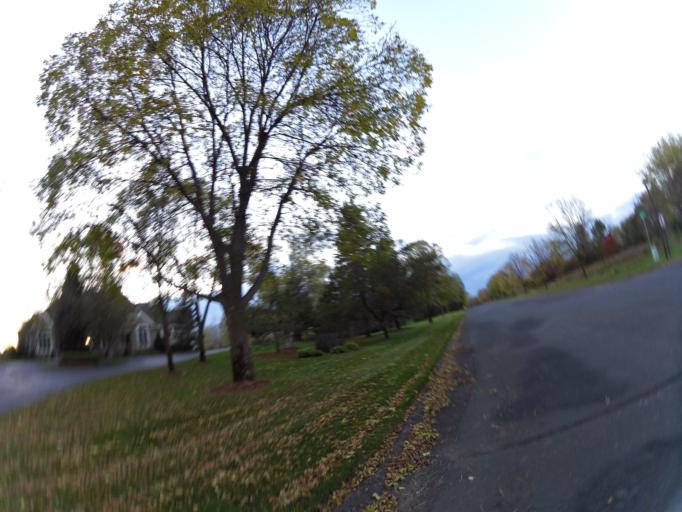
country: US
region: Minnesota
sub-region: Washington County
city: Lakeland
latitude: 44.9583
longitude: -92.8211
